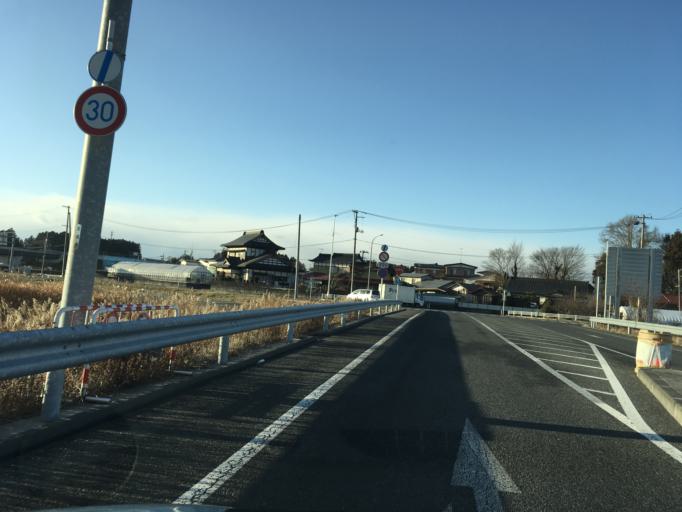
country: JP
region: Iwate
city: Ichinoseki
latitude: 38.7364
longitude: 141.1272
